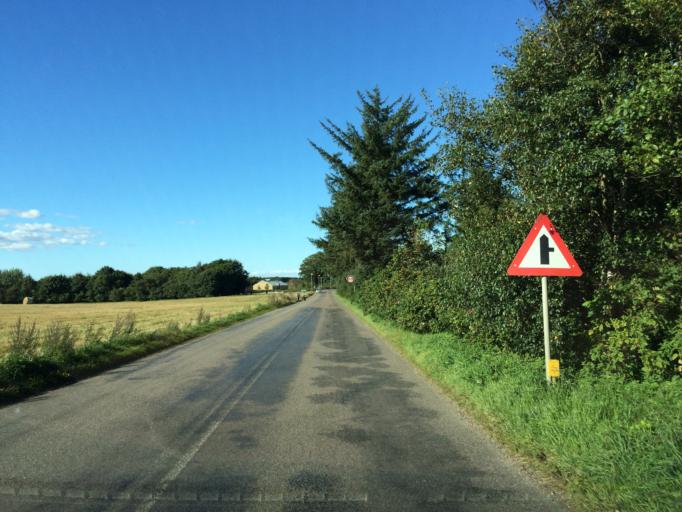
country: DK
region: Central Jutland
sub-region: Holstebro Kommune
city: Holstebro
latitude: 56.3147
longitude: 8.6216
